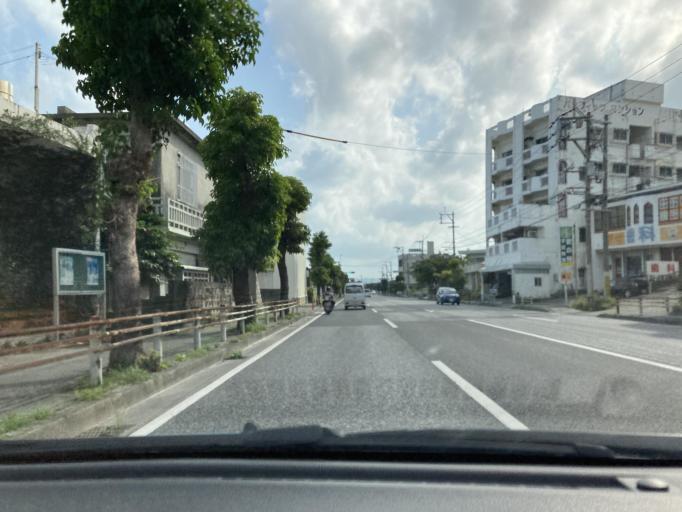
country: JP
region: Okinawa
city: Ginowan
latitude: 26.2673
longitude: 127.7906
